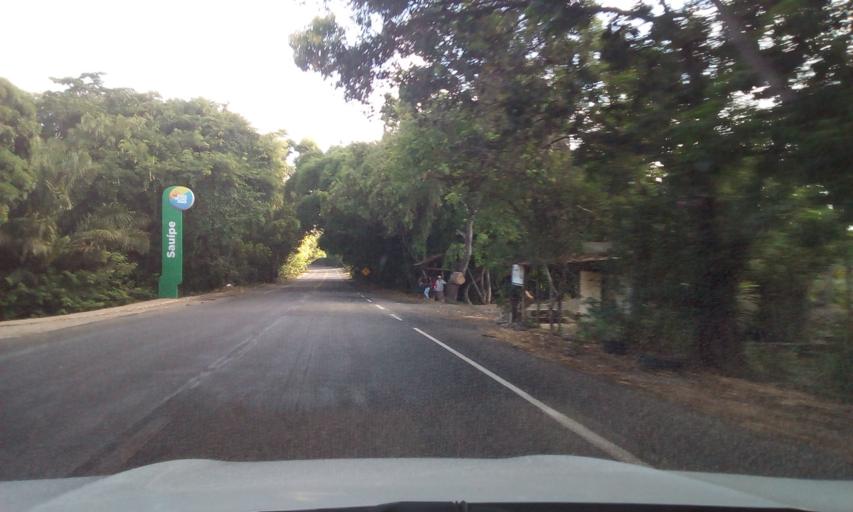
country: BR
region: Bahia
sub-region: Mata De Sao Joao
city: Mata de Sao Joao
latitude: -12.3939
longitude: -37.9152
